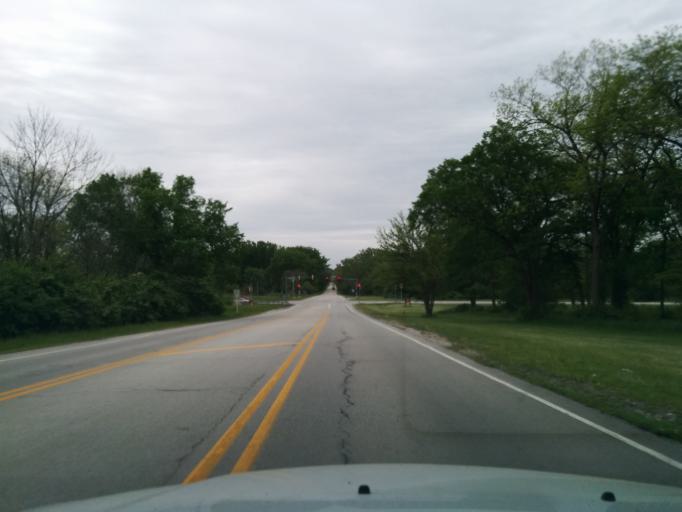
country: US
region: Illinois
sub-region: Cook County
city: Willow Springs
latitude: 41.6974
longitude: -87.8752
